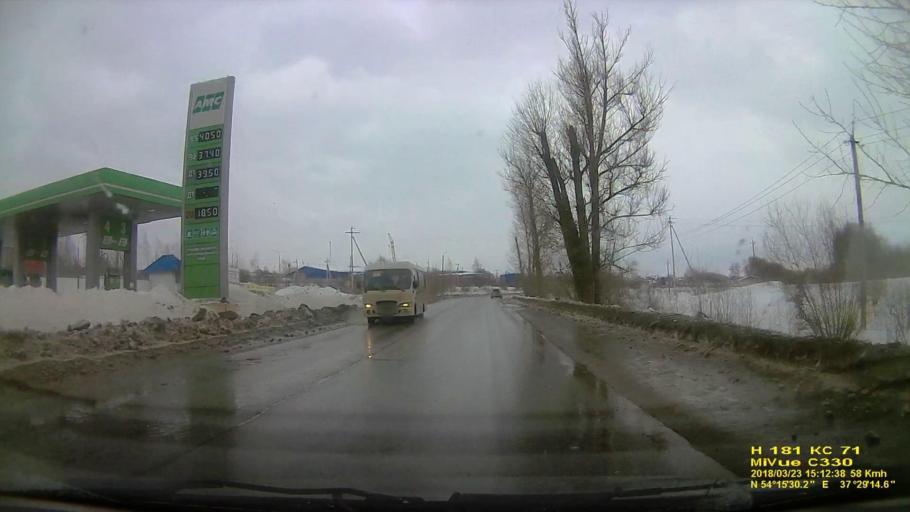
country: RU
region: Tula
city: Barsuki
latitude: 54.2583
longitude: 37.4874
